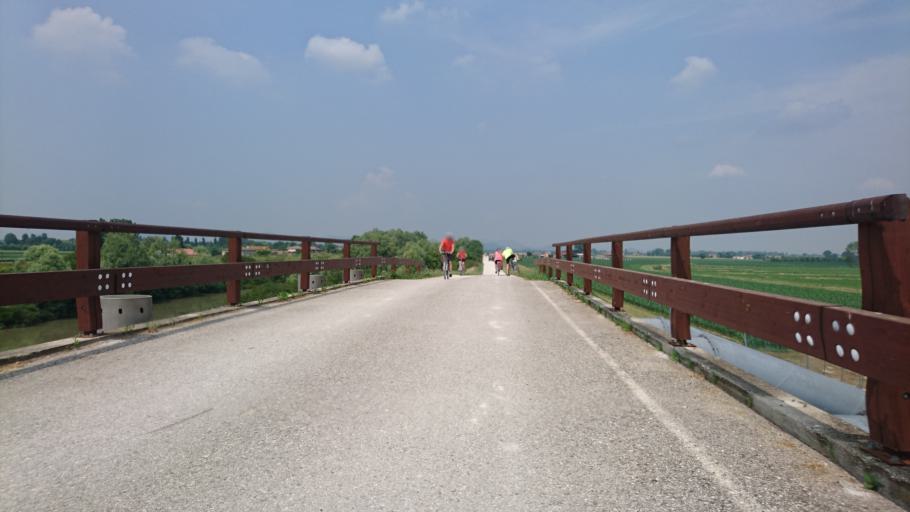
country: IT
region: Veneto
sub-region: Provincia di Padova
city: Bovolenta
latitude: 45.2730
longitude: 11.9229
